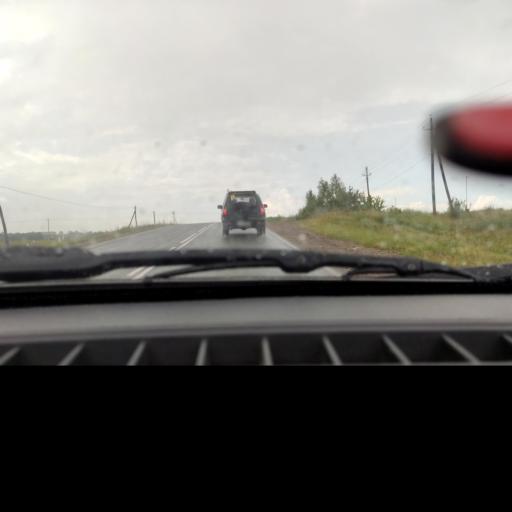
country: RU
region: Bashkortostan
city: Kabakovo
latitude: 54.5899
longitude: 56.2460
